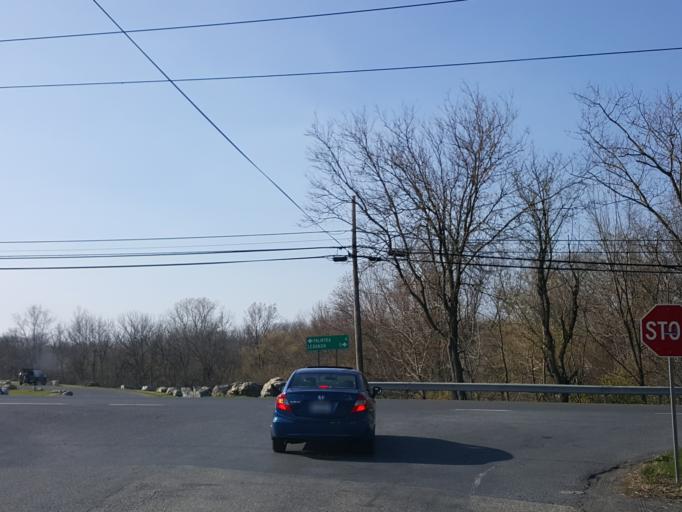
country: US
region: Pennsylvania
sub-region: Lebanon County
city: Annville
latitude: 40.3270
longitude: -76.5263
